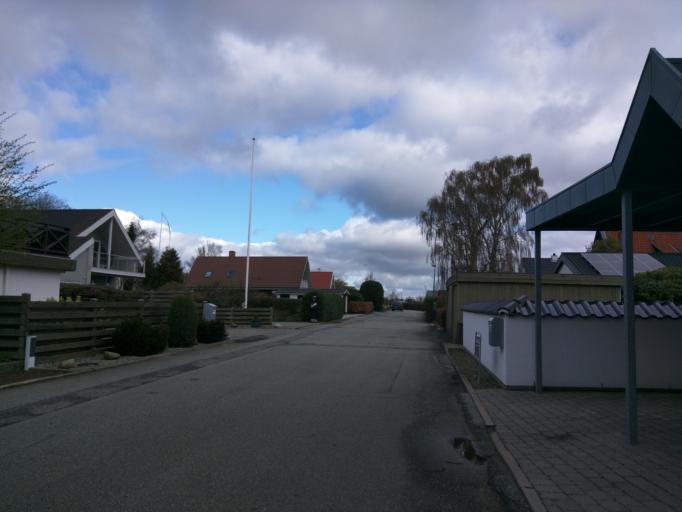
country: DK
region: South Denmark
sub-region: Fredericia Kommune
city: Snoghoj
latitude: 55.5474
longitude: 9.7280
